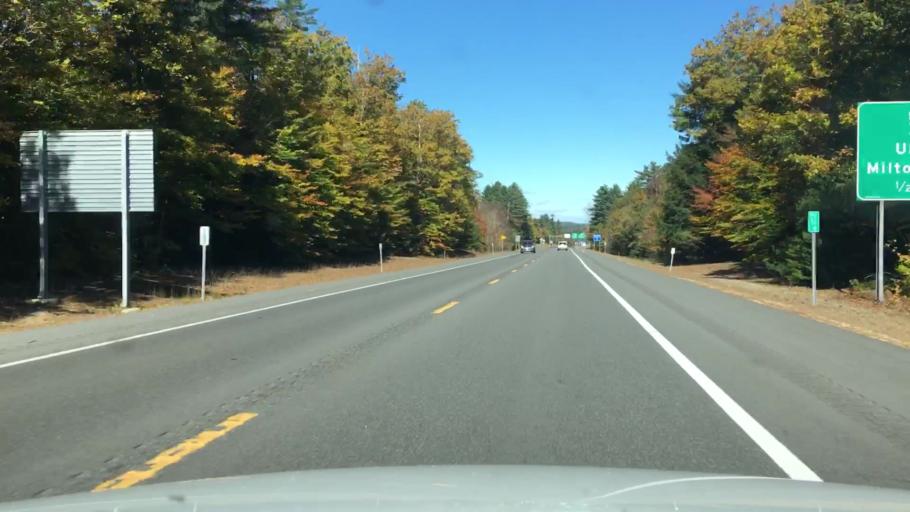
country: US
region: New Hampshire
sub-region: Carroll County
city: Sanbornville
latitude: 43.4699
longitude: -71.0000
